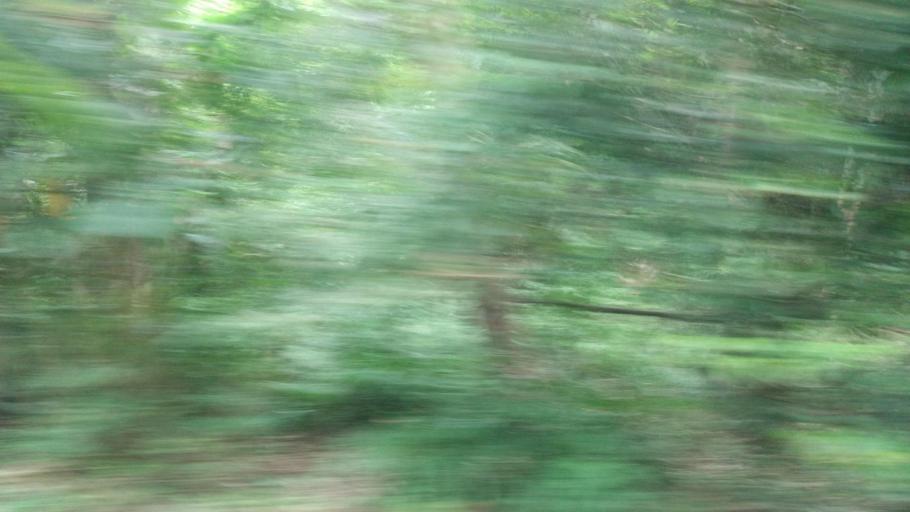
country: TW
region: Taiwan
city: Daxi
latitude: 24.9115
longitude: 121.3917
